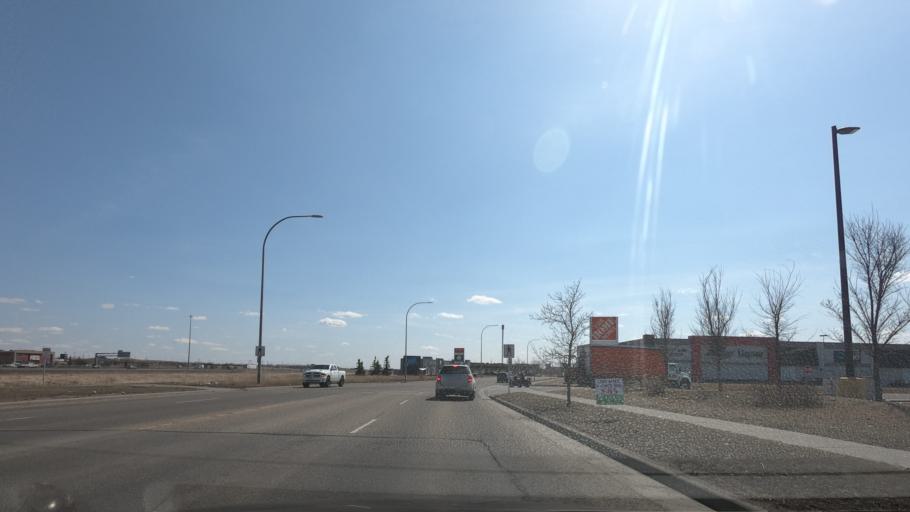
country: CA
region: Alberta
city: Airdrie
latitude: 51.2619
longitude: -114.0038
